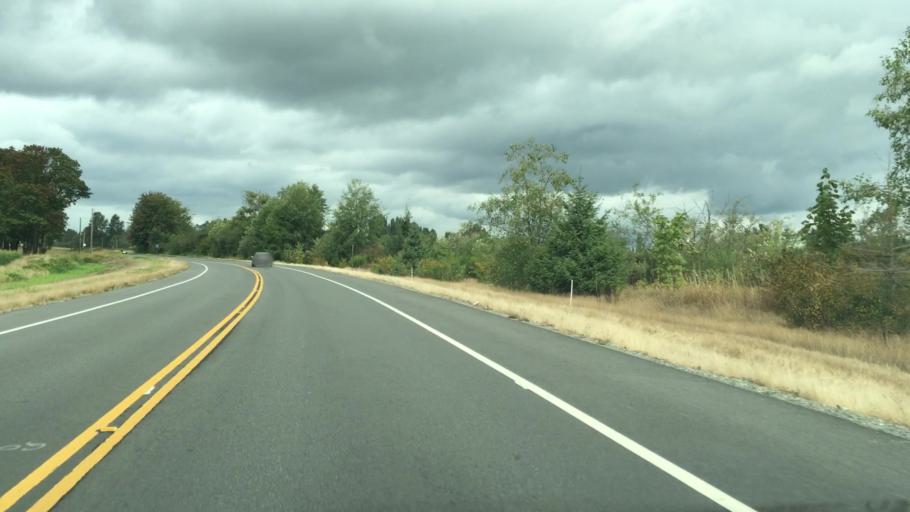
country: US
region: Washington
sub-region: Snohomish County
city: Everett
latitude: 47.9407
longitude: -122.1723
